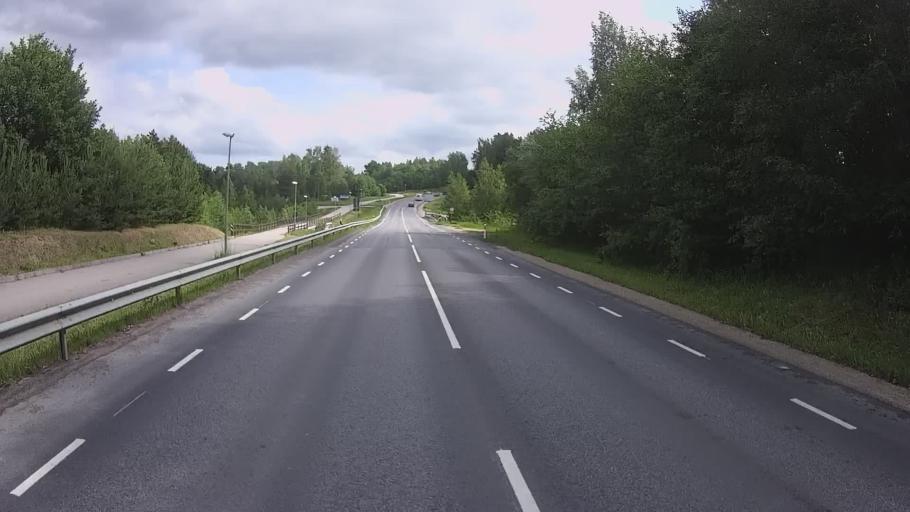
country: EE
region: Polvamaa
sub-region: Polva linn
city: Polva
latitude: 58.0673
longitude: 27.0607
